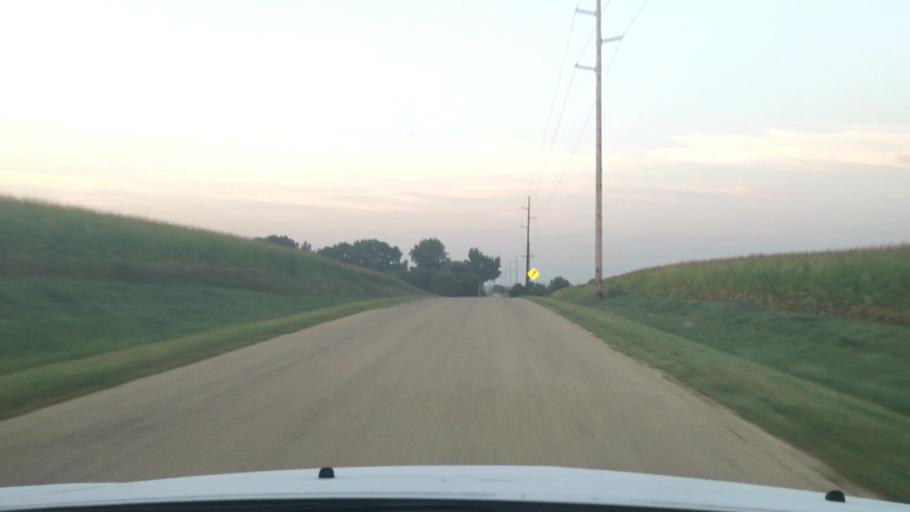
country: US
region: Illinois
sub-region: Ogle County
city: Rochelle
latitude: 41.8866
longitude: -89.0009
